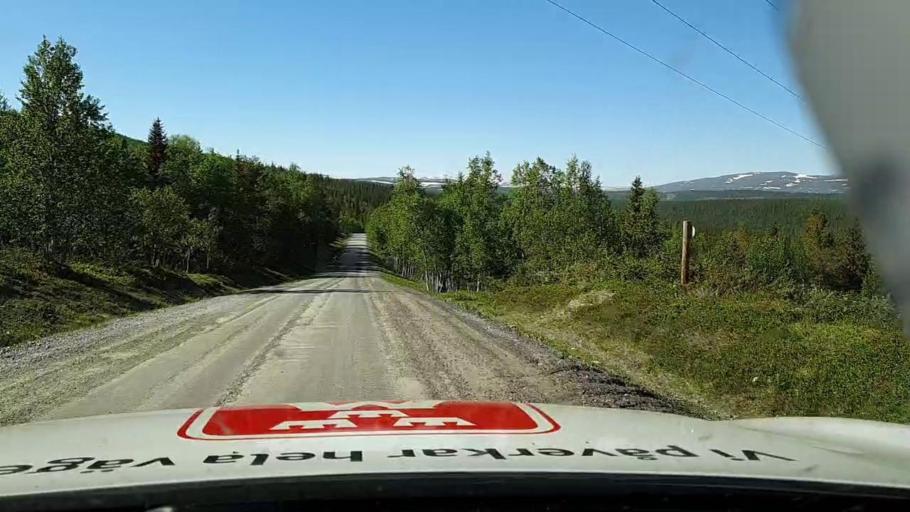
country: SE
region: Jaemtland
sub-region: Are Kommun
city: Are
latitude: 62.7920
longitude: 12.7645
